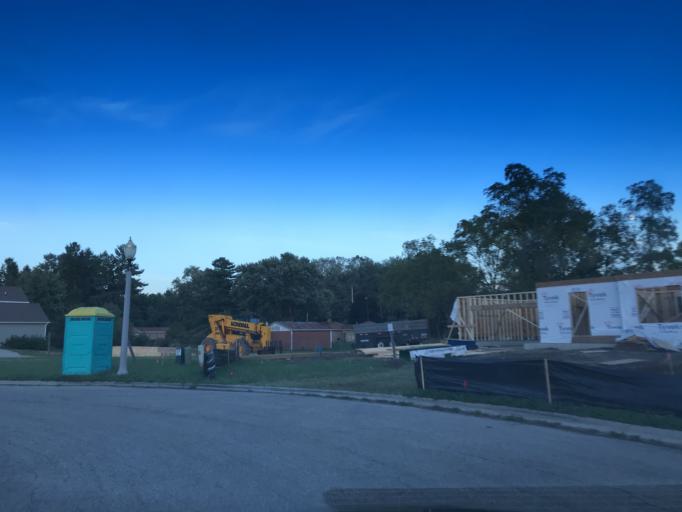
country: US
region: Michigan
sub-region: Eaton County
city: Waverly
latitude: 42.6933
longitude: -84.6329
